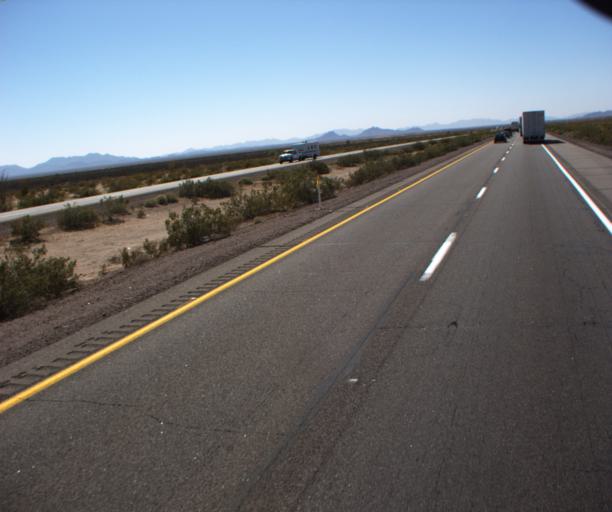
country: US
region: Arizona
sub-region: Yuma County
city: Wellton
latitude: 32.7170
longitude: -113.7997
